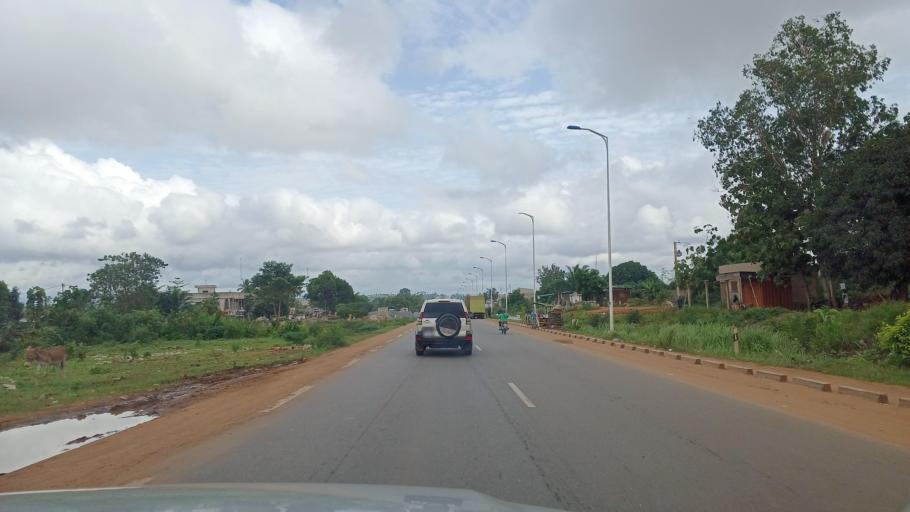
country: TG
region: Maritime
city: Tsevie
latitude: 6.3426
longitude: 1.2149
